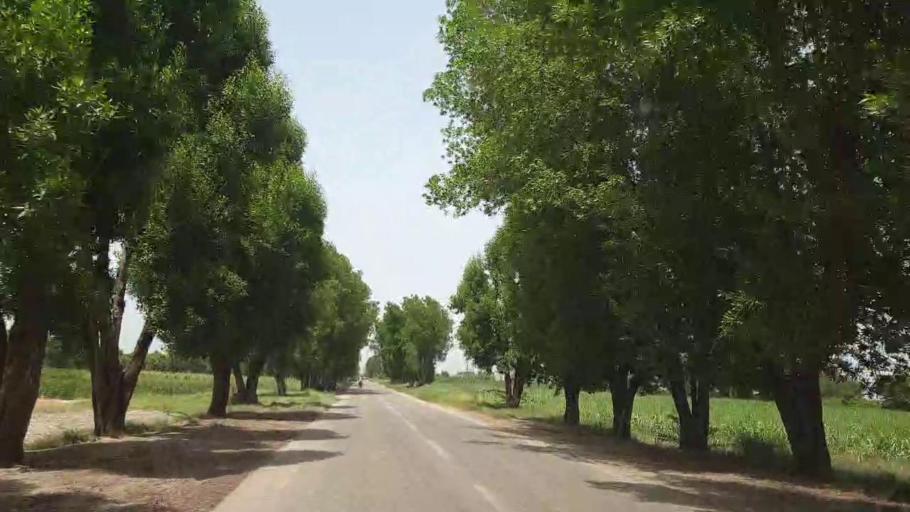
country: PK
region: Sindh
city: Sakrand
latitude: 26.1883
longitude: 68.2338
